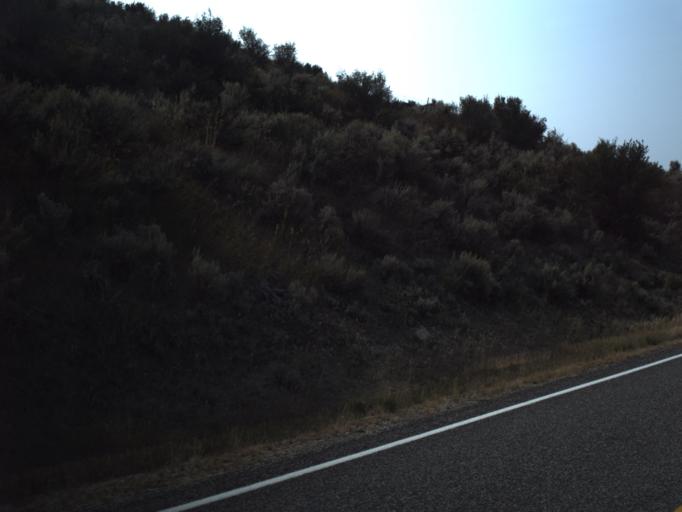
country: US
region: Utah
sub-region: Morgan County
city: Morgan
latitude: 40.9663
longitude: -111.5443
